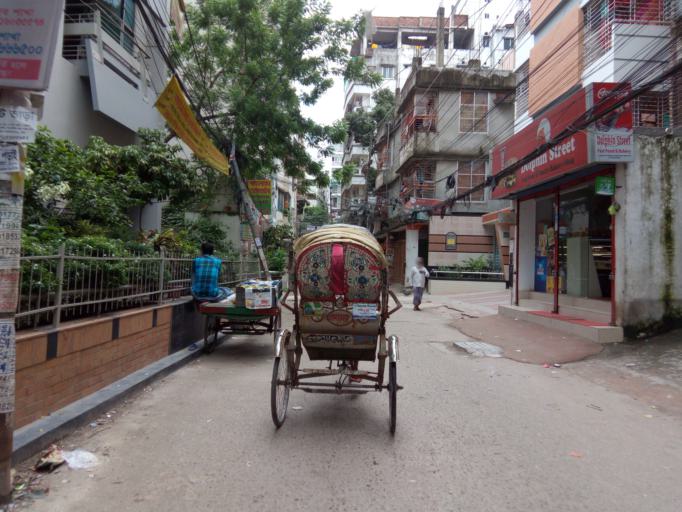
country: BD
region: Dhaka
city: Azimpur
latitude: 23.7509
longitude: 90.3797
